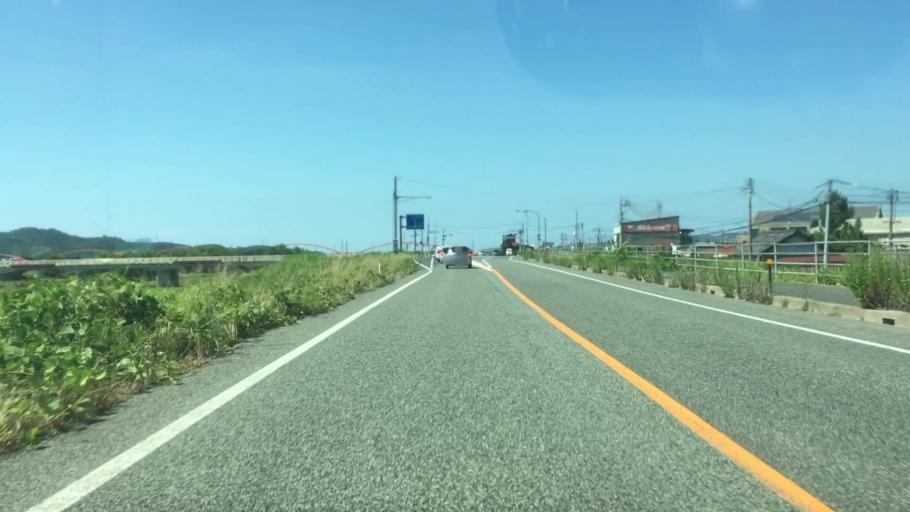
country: JP
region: Tottori
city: Tottori
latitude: 35.4627
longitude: 134.2149
